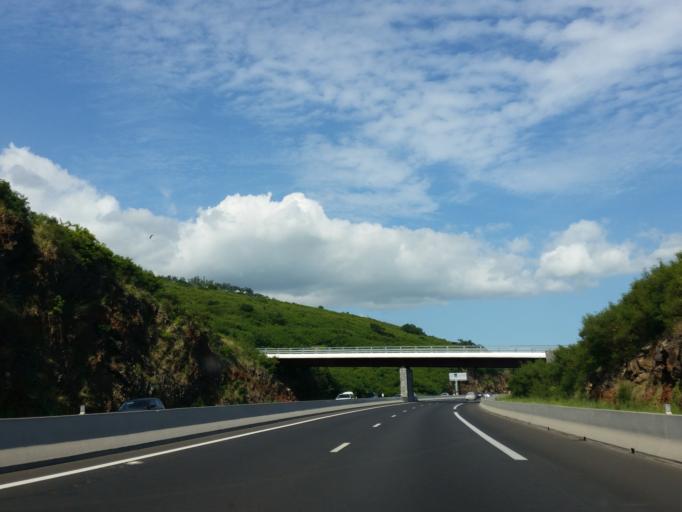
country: RE
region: Reunion
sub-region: Reunion
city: Trois-Bassins
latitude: -21.1262
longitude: 55.2814
